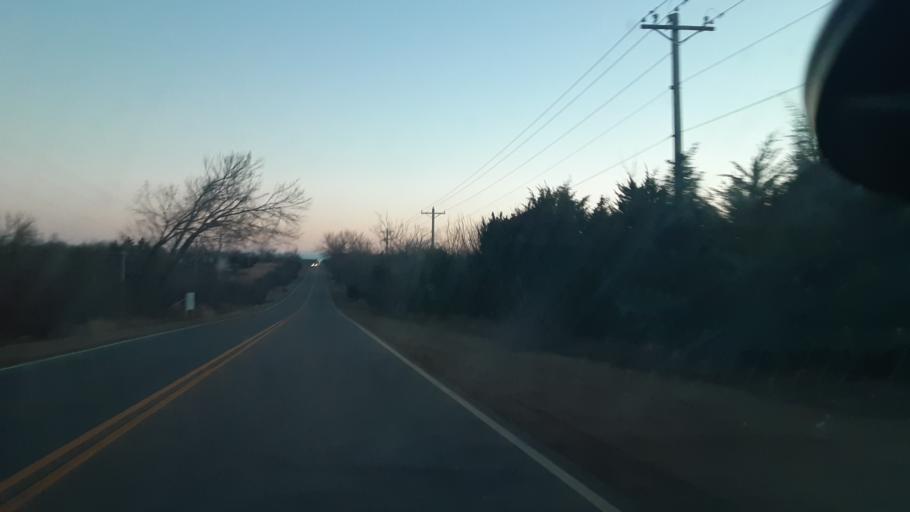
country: US
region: Oklahoma
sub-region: Oklahoma County
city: Edmond
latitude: 35.7044
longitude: -97.4253
